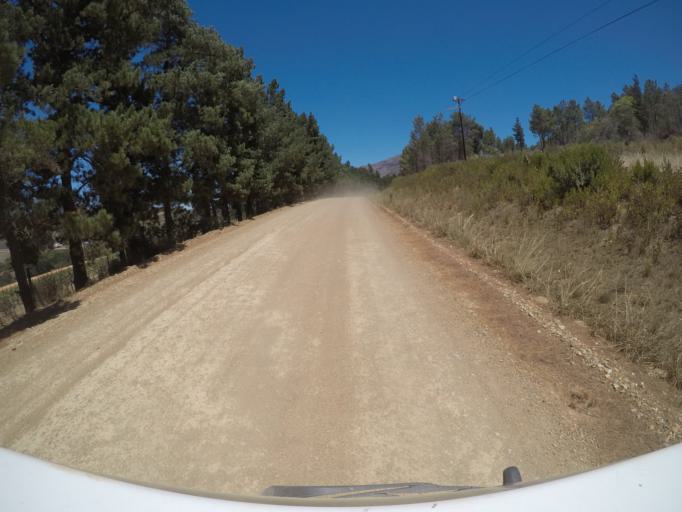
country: ZA
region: Western Cape
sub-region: Overberg District Municipality
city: Caledon
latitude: -34.1736
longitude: 19.2282
